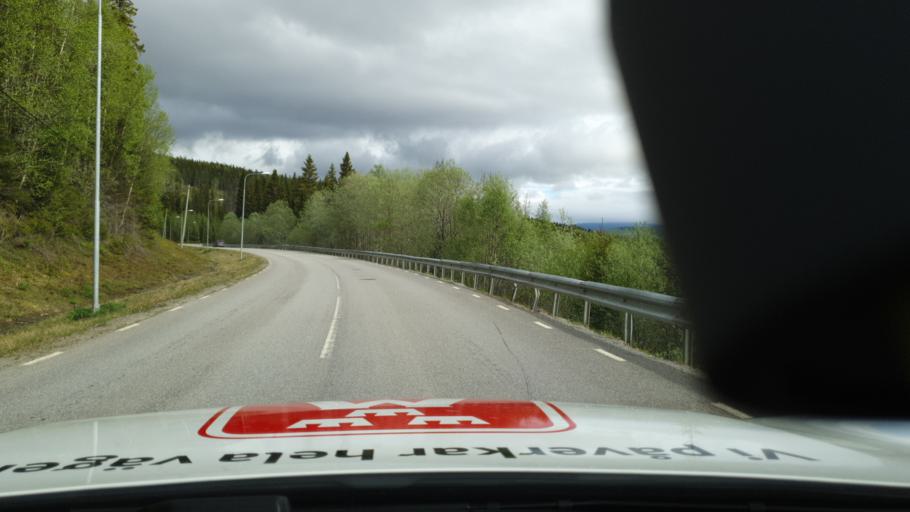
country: NO
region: Nord-Trondelag
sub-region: Lierne
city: Sandvika
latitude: 64.4870
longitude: 14.1358
